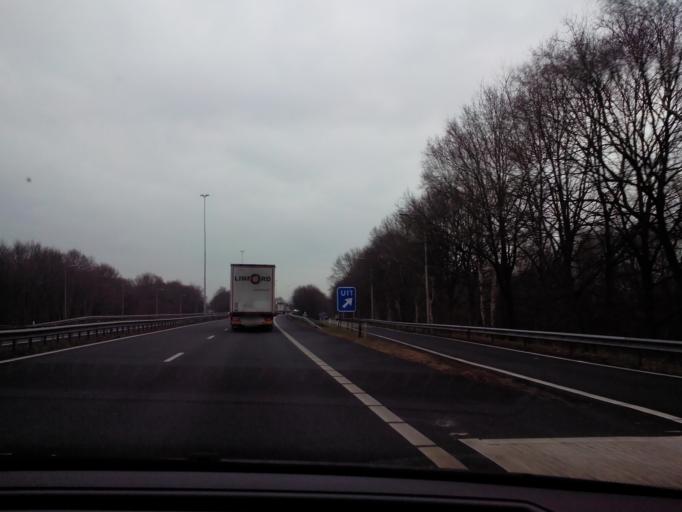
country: NL
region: North Brabant
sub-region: Gemeente Breda
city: Hoge Vucht
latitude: 51.5894
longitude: 4.8267
